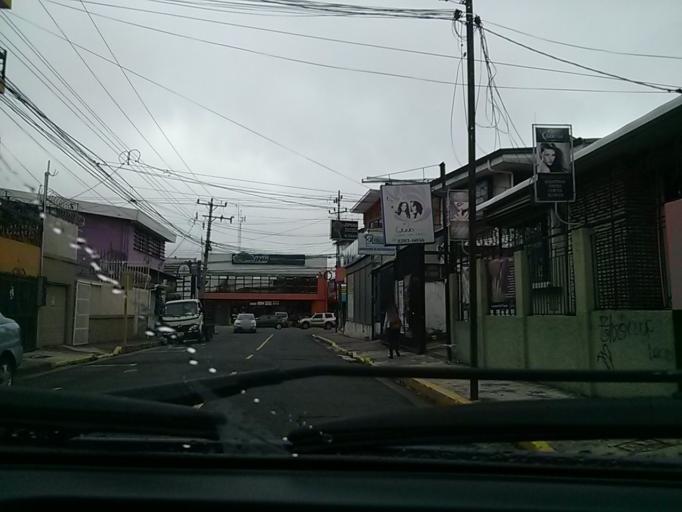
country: CR
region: San Jose
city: San Pedro
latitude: 9.9326
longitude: -84.0499
